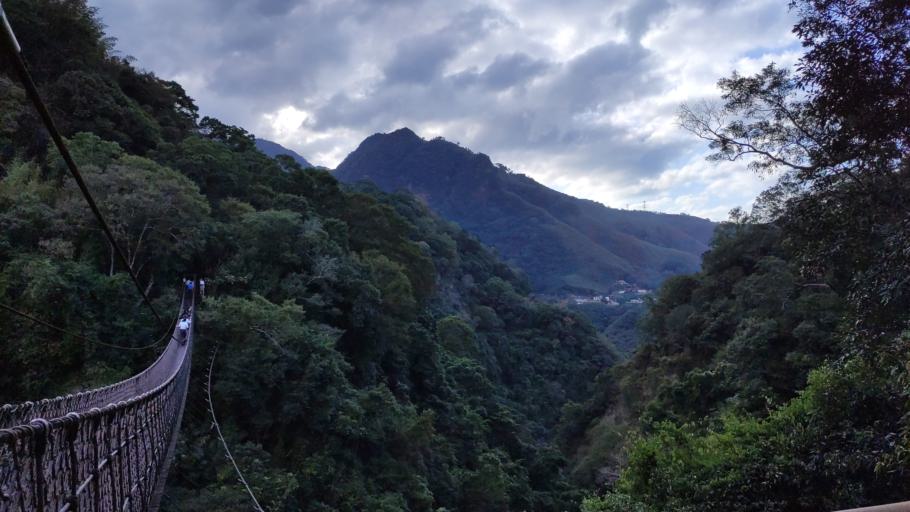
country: TW
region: Taiwan
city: Daxi
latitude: 24.7899
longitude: 121.3747
